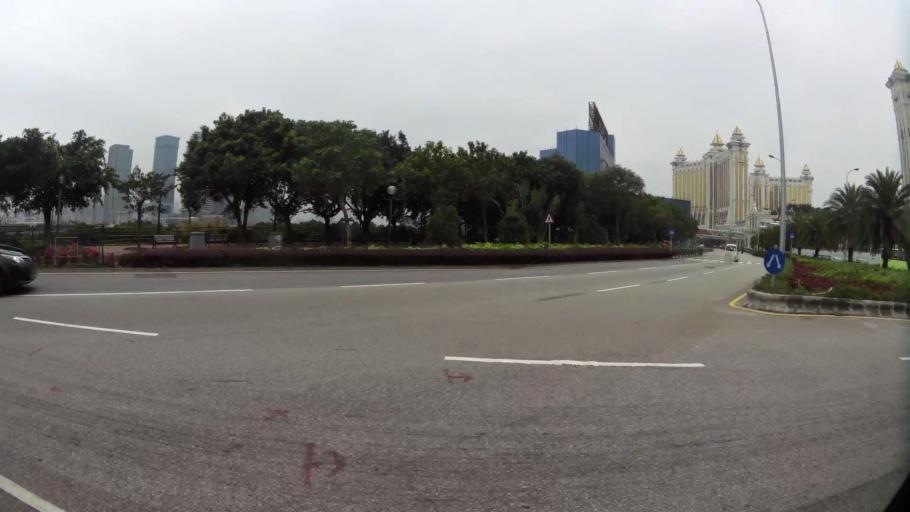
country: MO
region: Macau
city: Macau
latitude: 22.1437
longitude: 113.5523
